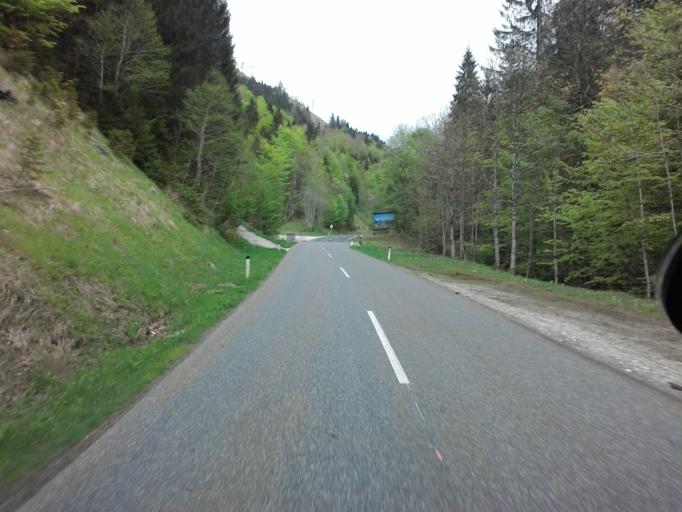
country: AT
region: Styria
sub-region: Politischer Bezirk Liezen
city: Hall
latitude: 47.7136
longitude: 14.4229
